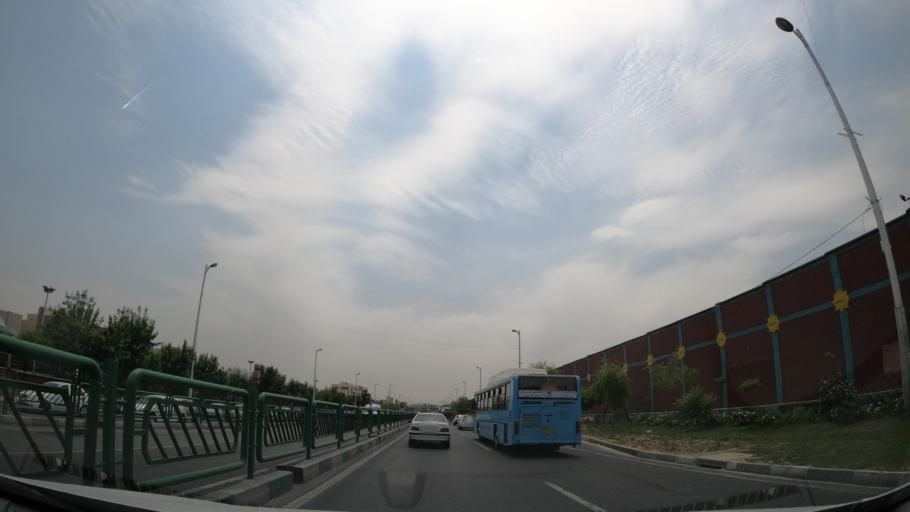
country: IR
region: Tehran
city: Tehran
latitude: 35.6929
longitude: 51.3404
